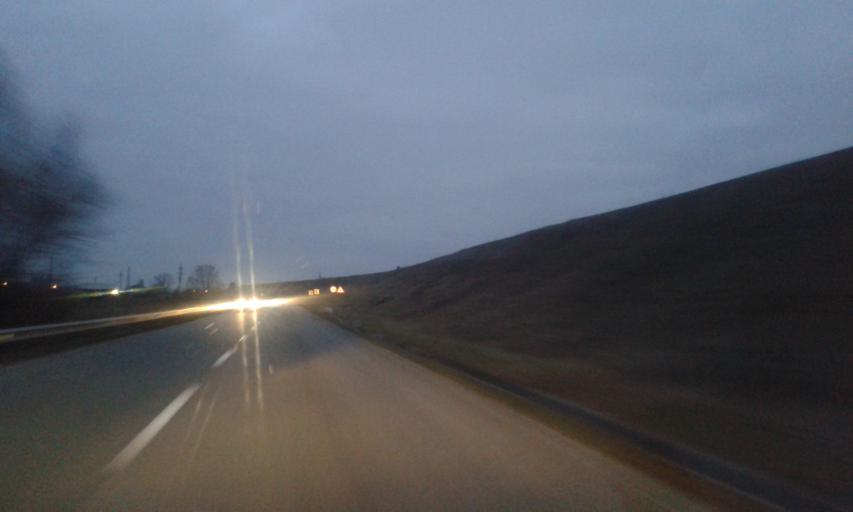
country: RO
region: Gorj
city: Targu Jiu
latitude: 45.0631
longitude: 23.2750
